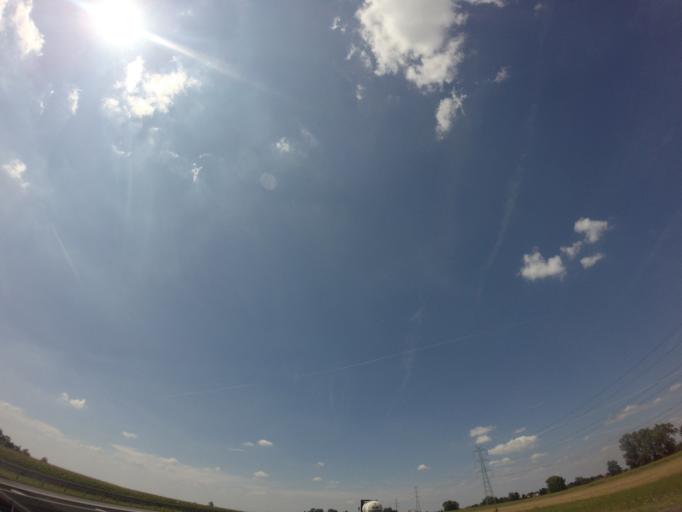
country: PL
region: Lower Silesian Voivodeship
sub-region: Powiat olawski
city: Wierzbno
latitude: 50.9136
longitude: 17.1464
